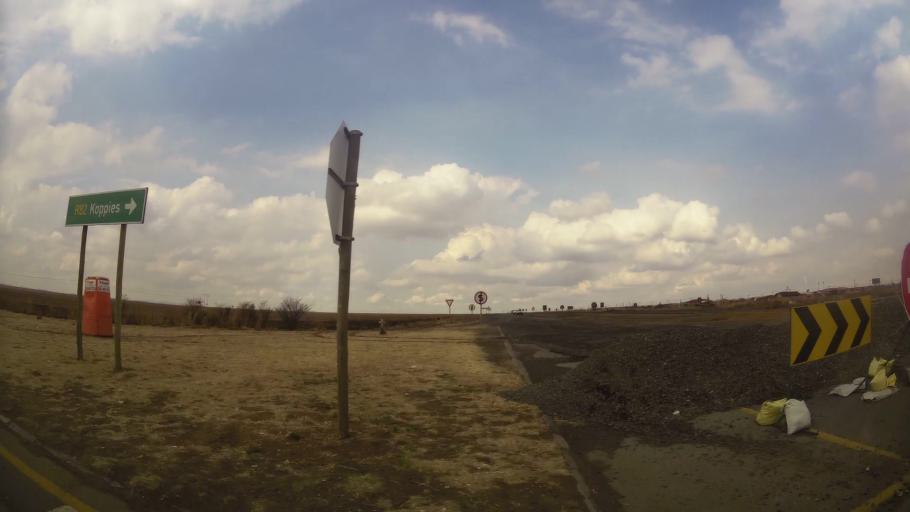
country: ZA
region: Orange Free State
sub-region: Fezile Dabi District Municipality
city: Sasolburg
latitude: -26.8466
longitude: 27.8897
